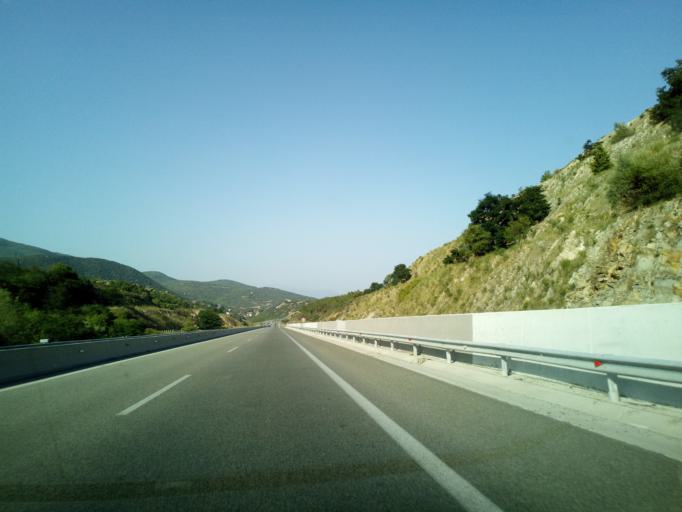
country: GR
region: Central Macedonia
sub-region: Nomos Thessalonikis
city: Nea Vrasna
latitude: 40.6950
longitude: 23.6348
